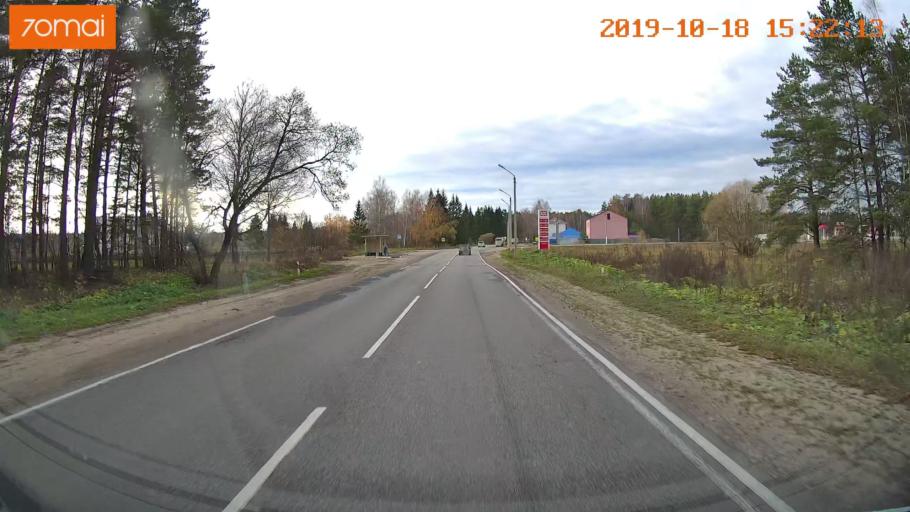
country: RU
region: Vladimir
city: Anopino
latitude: 55.7064
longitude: 40.7353
